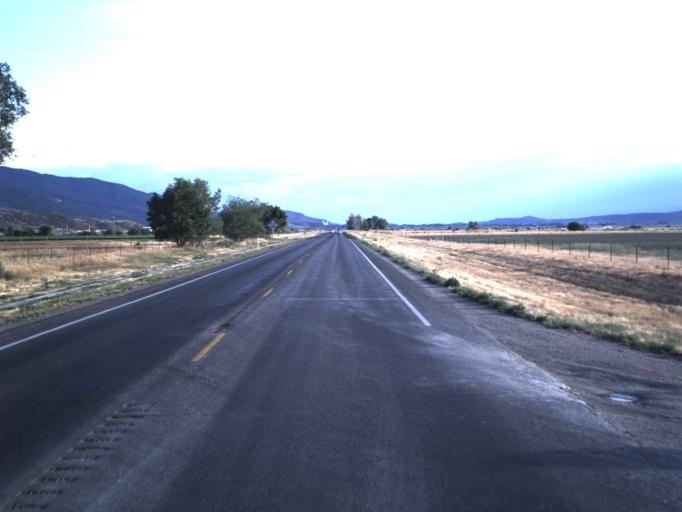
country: US
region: Utah
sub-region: Sanpete County
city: Ephraim
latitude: 39.3375
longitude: -111.5959
